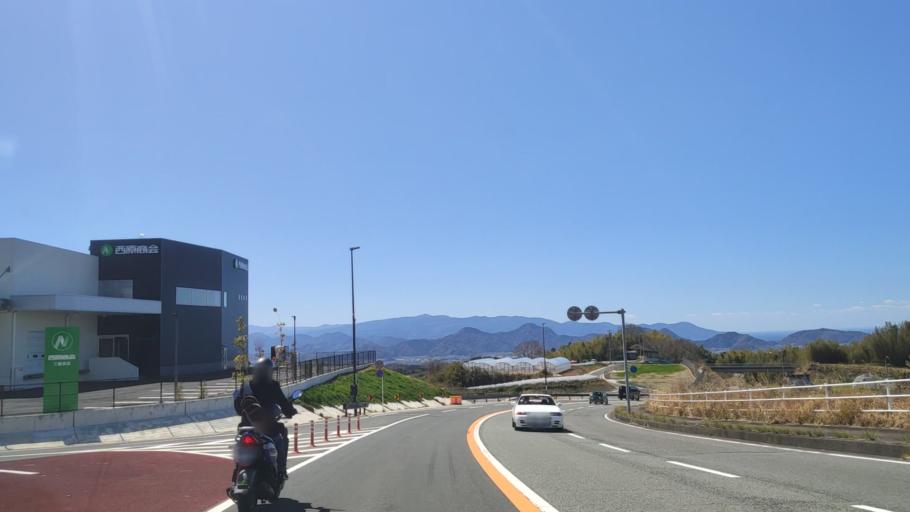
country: JP
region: Shizuoka
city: Mishima
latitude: 35.1370
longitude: 138.9693
